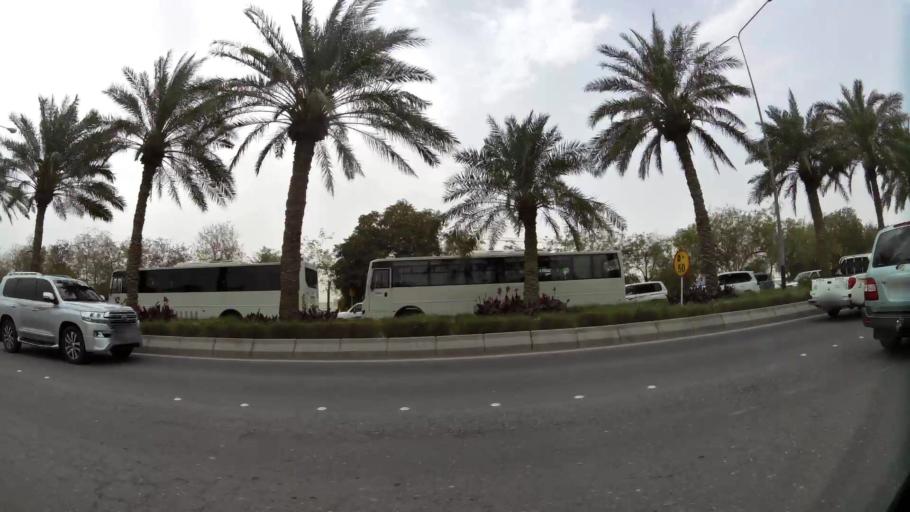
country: QA
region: Baladiyat ad Dawhah
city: Doha
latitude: 25.2930
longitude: 51.4928
